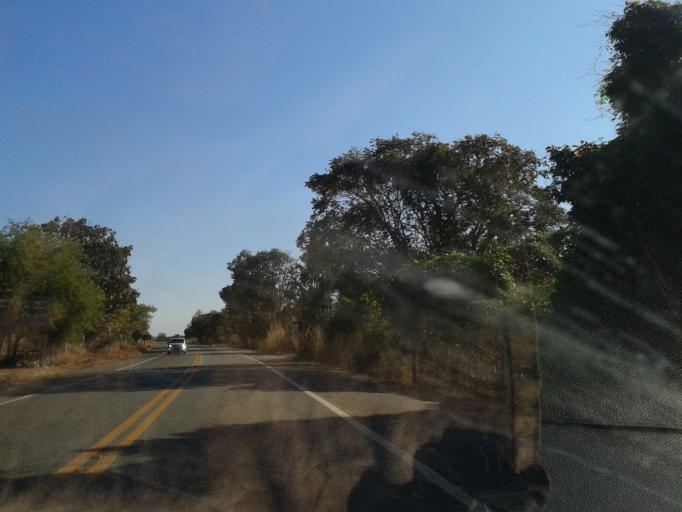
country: BR
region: Goias
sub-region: Mozarlandia
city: Mozarlandia
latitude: -14.8033
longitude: -50.5337
